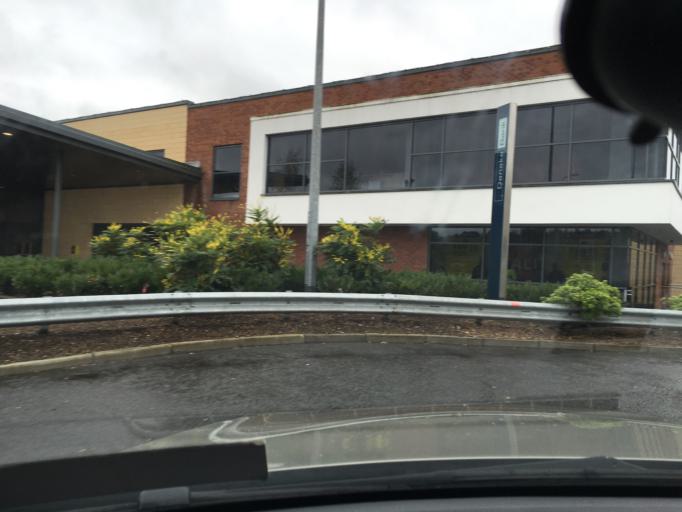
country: GB
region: Northern Ireland
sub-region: City of Belfast
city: Belfast
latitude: 54.5822
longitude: -5.9786
